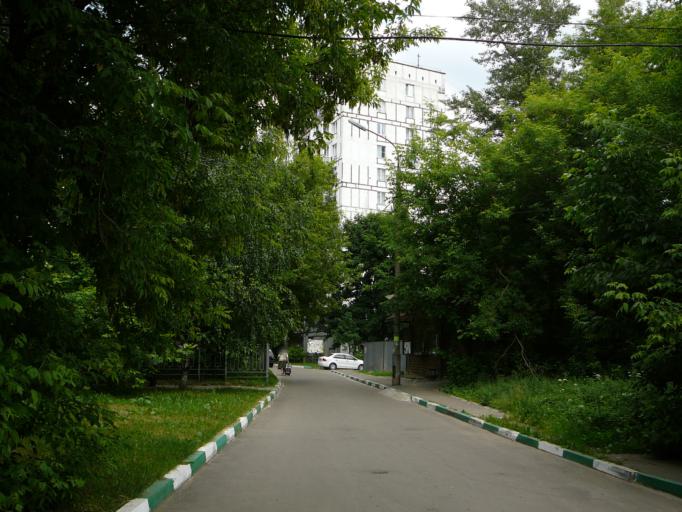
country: RU
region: Moskovskaya
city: Krasnogorsk
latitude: 55.8128
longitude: 37.3074
